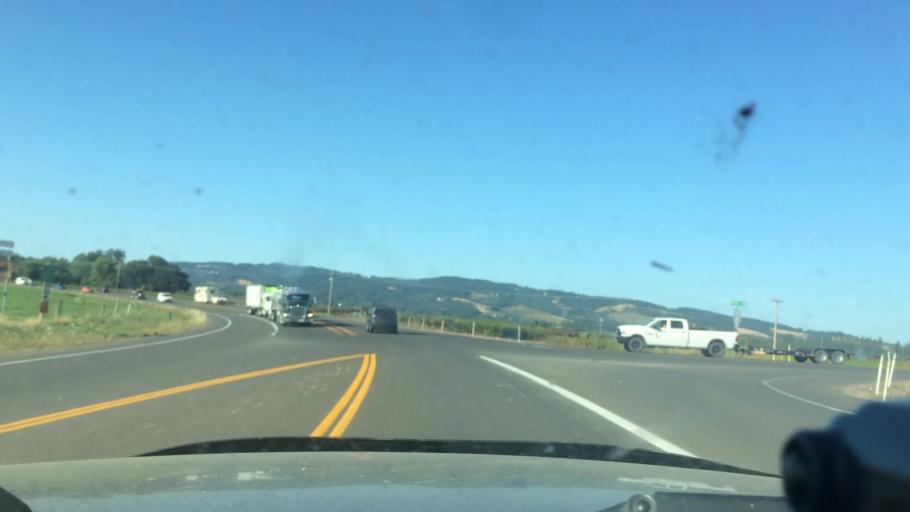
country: US
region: Oregon
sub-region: Yamhill County
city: Newberg
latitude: 45.2447
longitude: -122.9433
